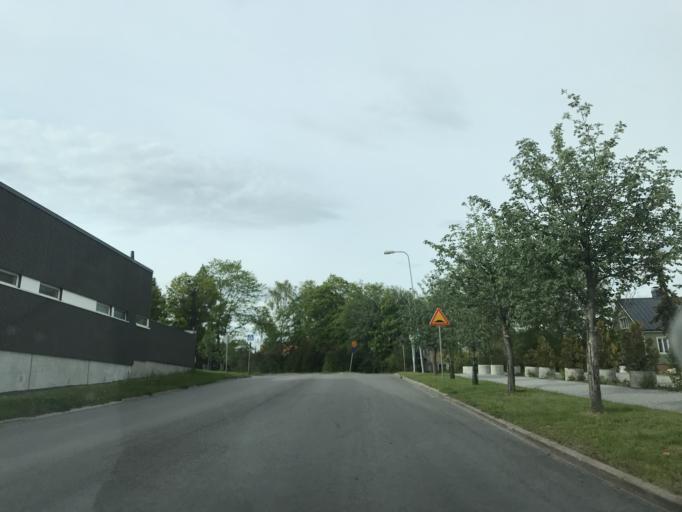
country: FI
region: Varsinais-Suomi
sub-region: Turku
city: Turku
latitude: 60.4502
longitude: 22.3088
